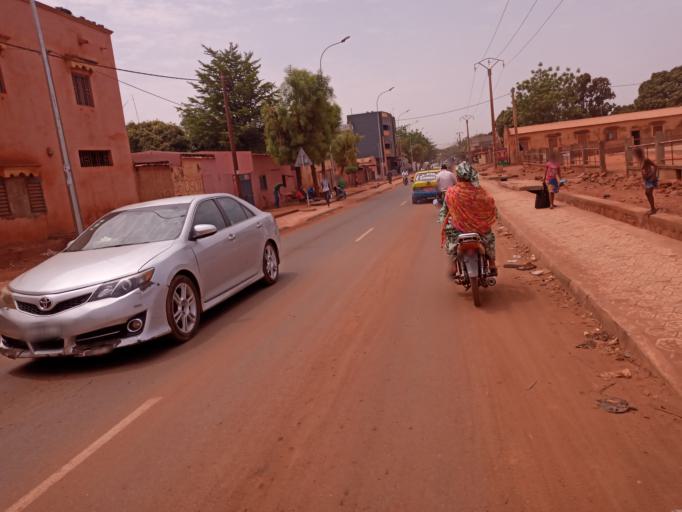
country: ML
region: Bamako
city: Bamako
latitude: 12.5833
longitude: -7.9882
